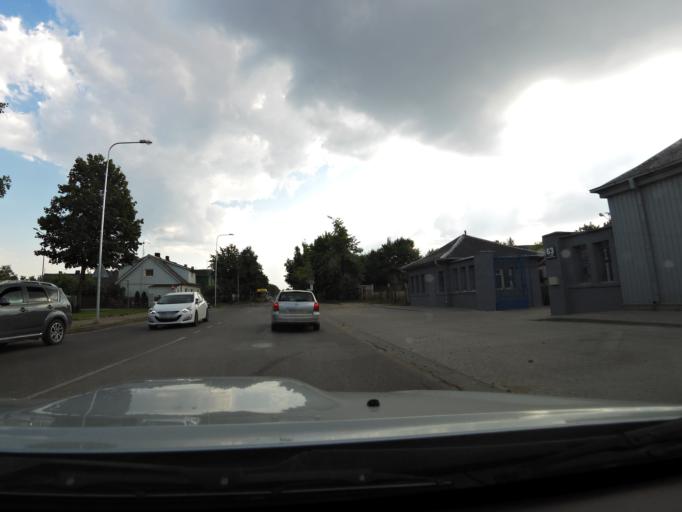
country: LT
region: Siauliu apskritis
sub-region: Siauliai
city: Siauliai
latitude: 55.9505
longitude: 23.3136
